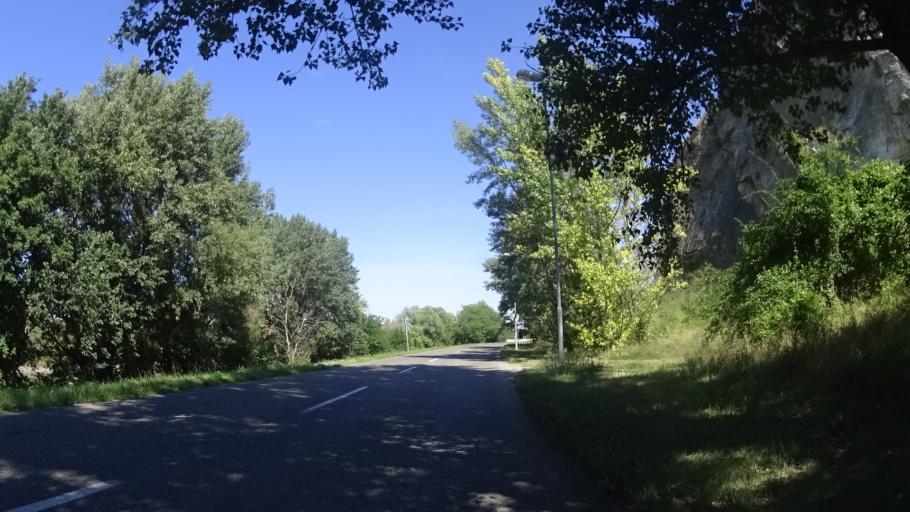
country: AT
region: Lower Austria
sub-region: Politischer Bezirk Bruck an der Leitha
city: Hainburg an der Donau
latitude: 48.2005
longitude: 16.9712
